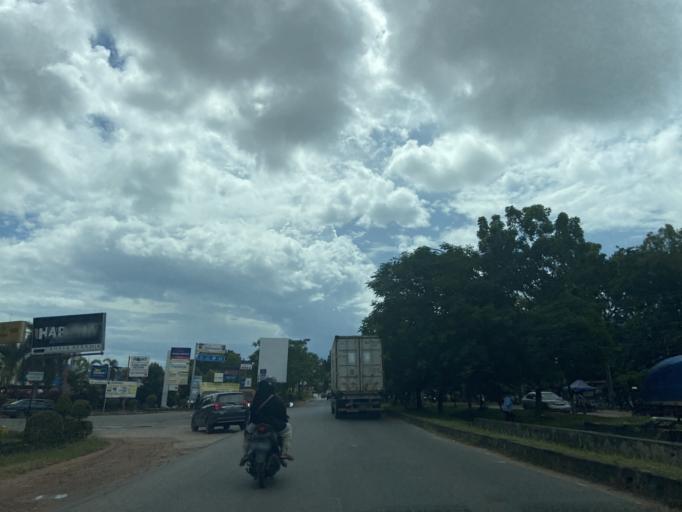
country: SG
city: Singapore
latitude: 1.0424
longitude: 103.9822
